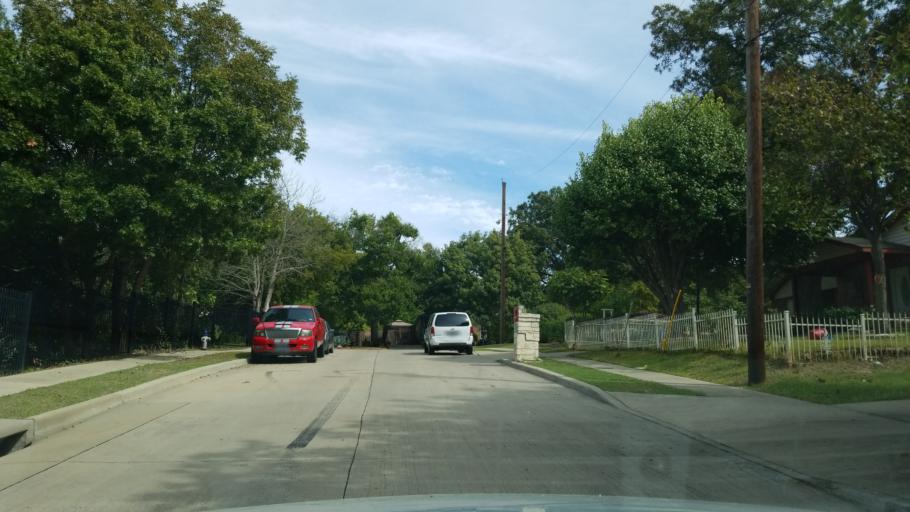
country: US
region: Texas
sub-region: Dallas County
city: Highland Park
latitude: 32.7856
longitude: -96.7214
